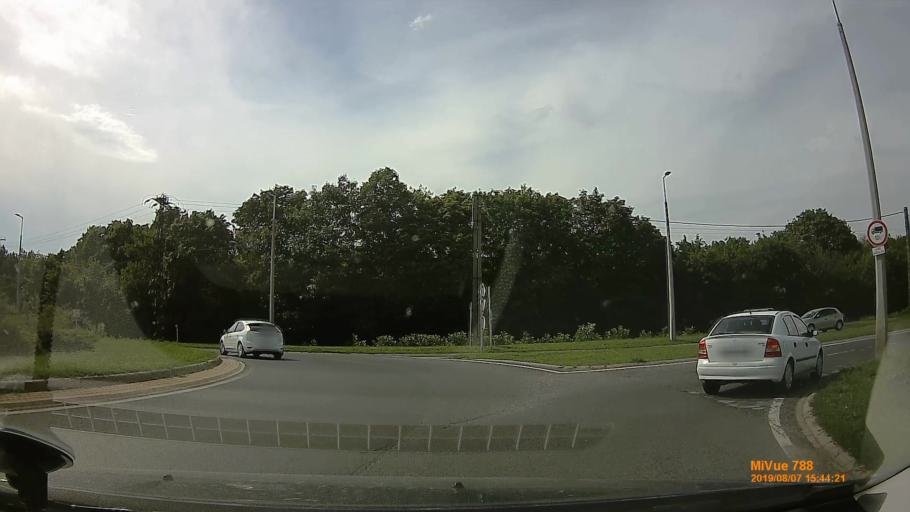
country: HU
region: Vas
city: Szombathely
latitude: 47.2085
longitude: 16.6174
